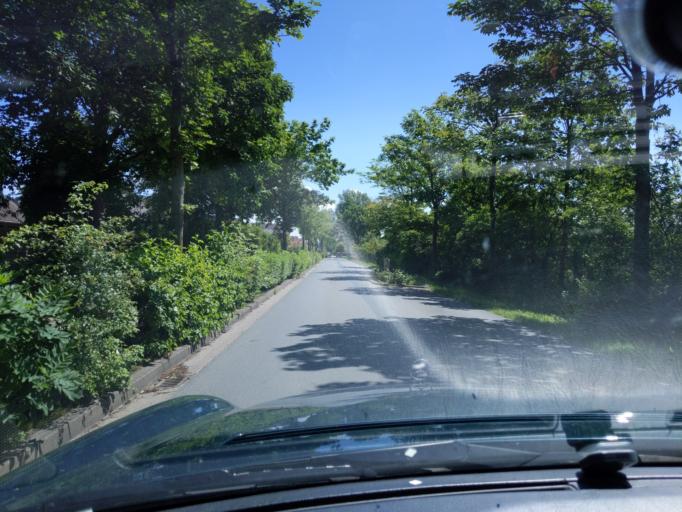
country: DE
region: Lower Saxony
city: Butjadingen
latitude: 53.5725
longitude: 8.2576
